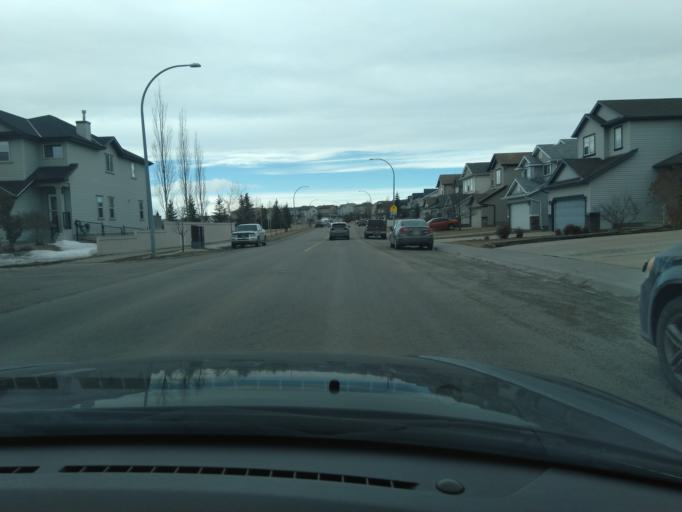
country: CA
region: Alberta
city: Calgary
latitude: 51.1690
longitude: -114.0587
